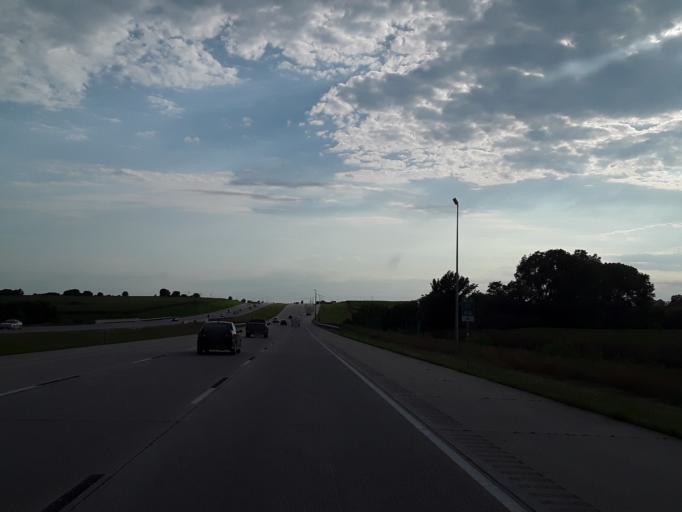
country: US
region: Nebraska
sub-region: Lancaster County
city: Waverly
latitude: 40.9295
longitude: -96.4466
